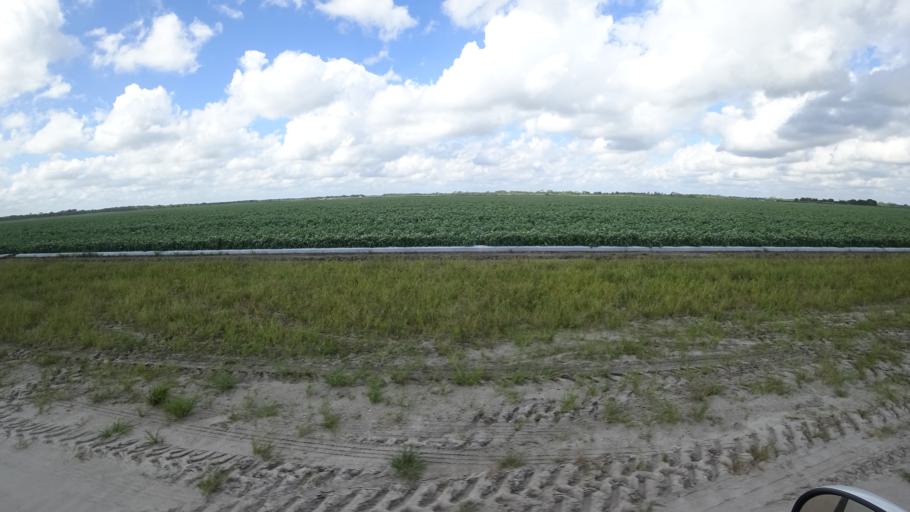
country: US
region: Florida
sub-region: Sarasota County
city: Lake Sarasota
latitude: 27.4094
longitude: -82.1998
